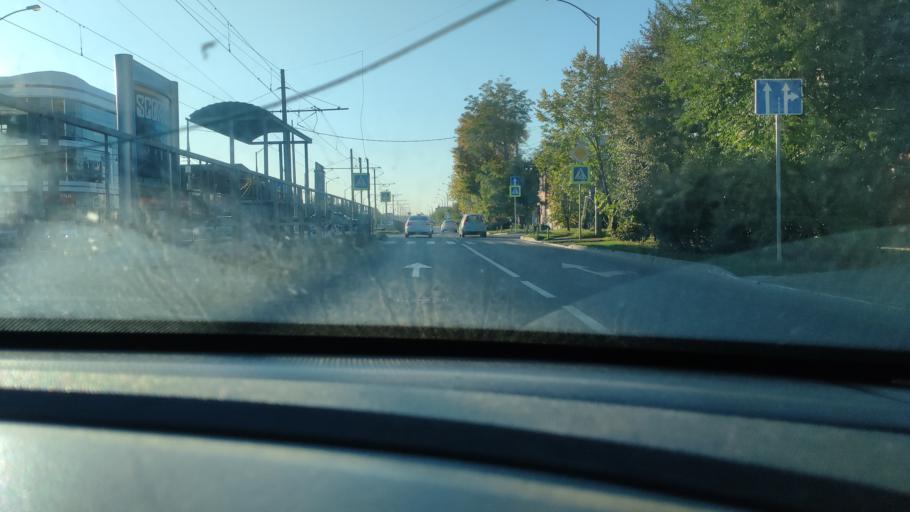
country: RU
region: Krasnodarskiy
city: Krasnodar
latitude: 45.0410
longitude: 38.9490
